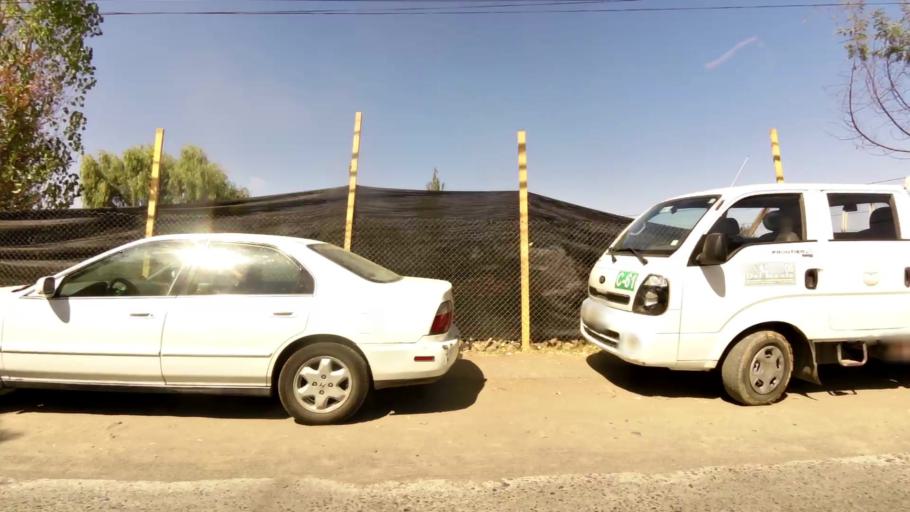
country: CL
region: Maule
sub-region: Provincia de Talca
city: Talca
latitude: -35.4156
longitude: -71.6489
